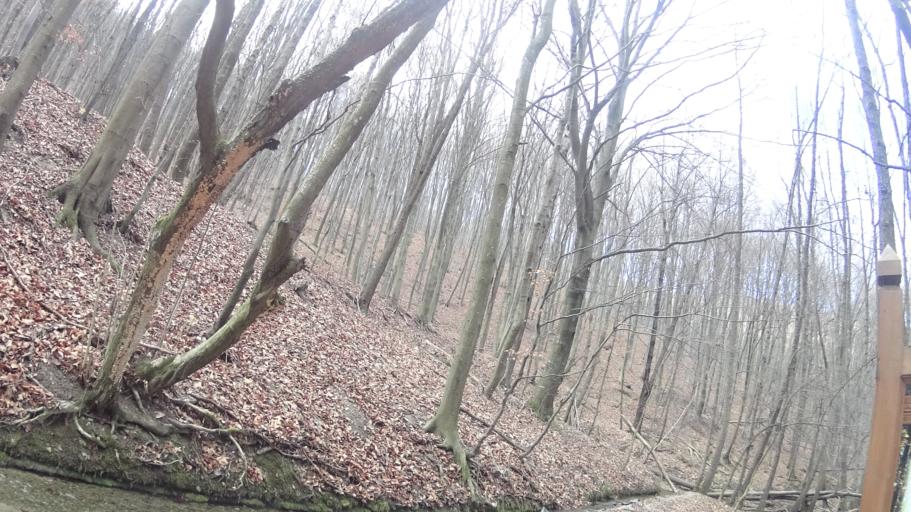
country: HU
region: Heves
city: Szilvasvarad
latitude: 48.0794
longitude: 20.4063
